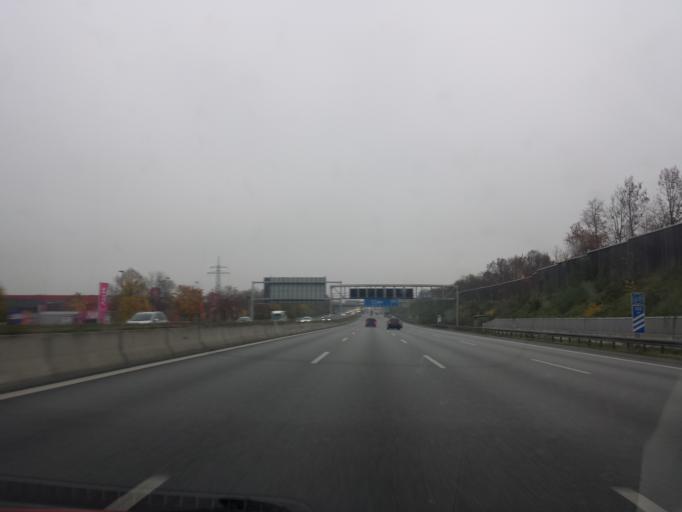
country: DE
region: Bavaria
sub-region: Upper Bavaria
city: Eching
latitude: 48.3044
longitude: 11.6282
